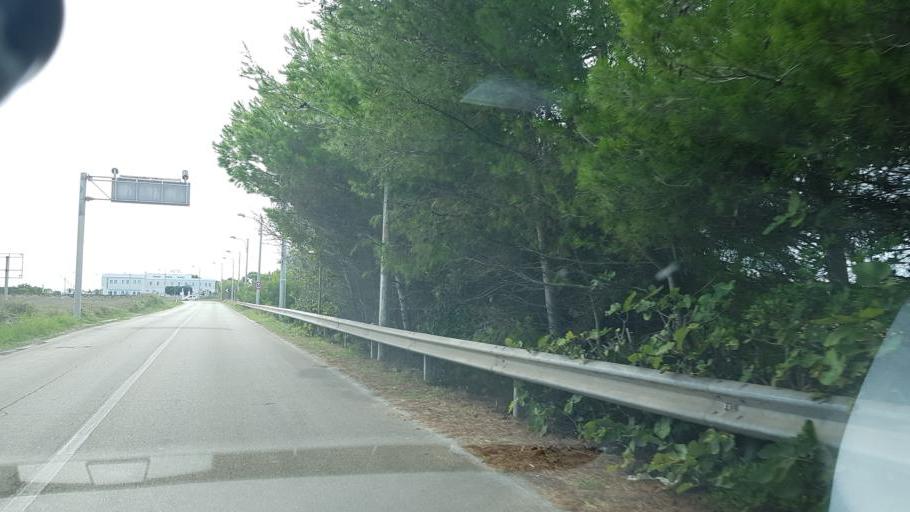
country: IT
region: Apulia
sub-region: Provincia di Lecce
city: Borgagne
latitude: 40.2891
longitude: 18.4238
